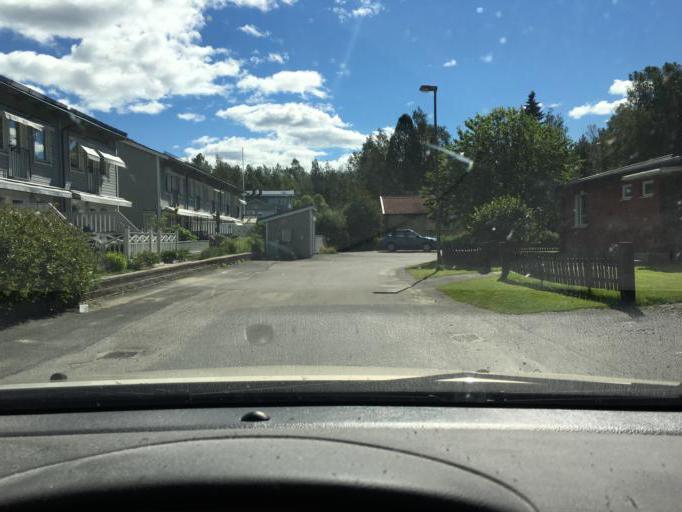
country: SE
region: Norrbotten
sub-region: Lulea Kommun
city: Lulea
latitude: 65.5956
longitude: 22.1365
